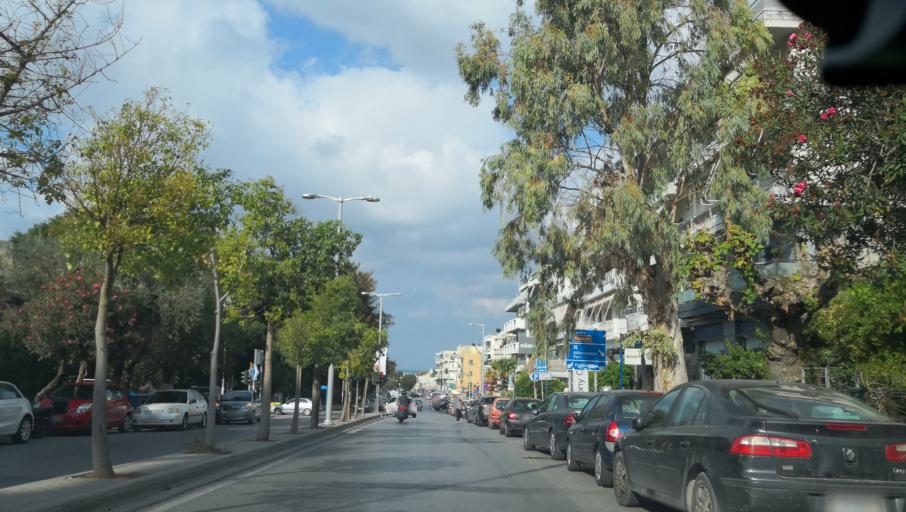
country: GR
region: Crete
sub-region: Nomos Irakleiou
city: Irakleion
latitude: 35.3342
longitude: 25.1387
